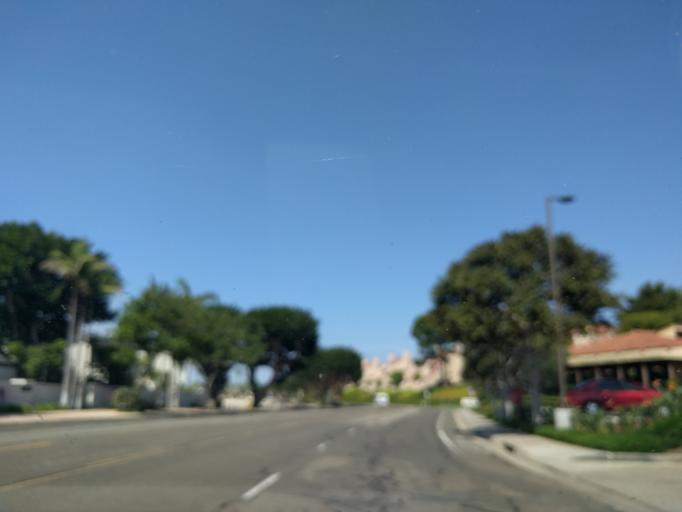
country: US
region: California
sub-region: Orange County
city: Newport Beach
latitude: 33.6111
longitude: -117.8933
